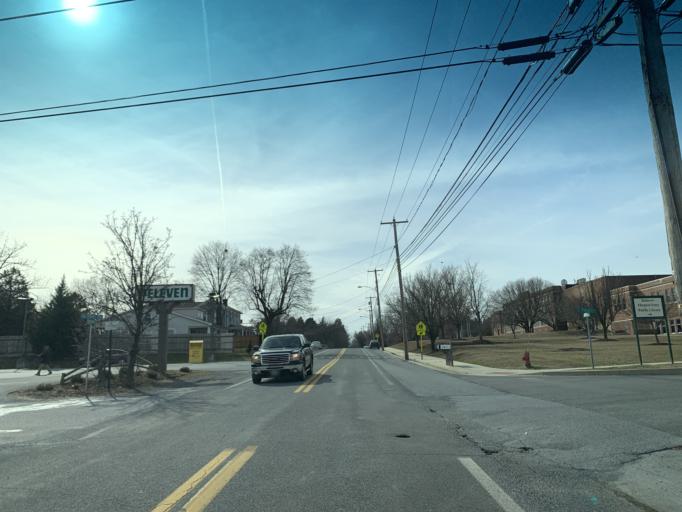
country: US
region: West Virginia
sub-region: Jefferson County
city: Bolivar
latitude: 39.3227
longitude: -77.7548
